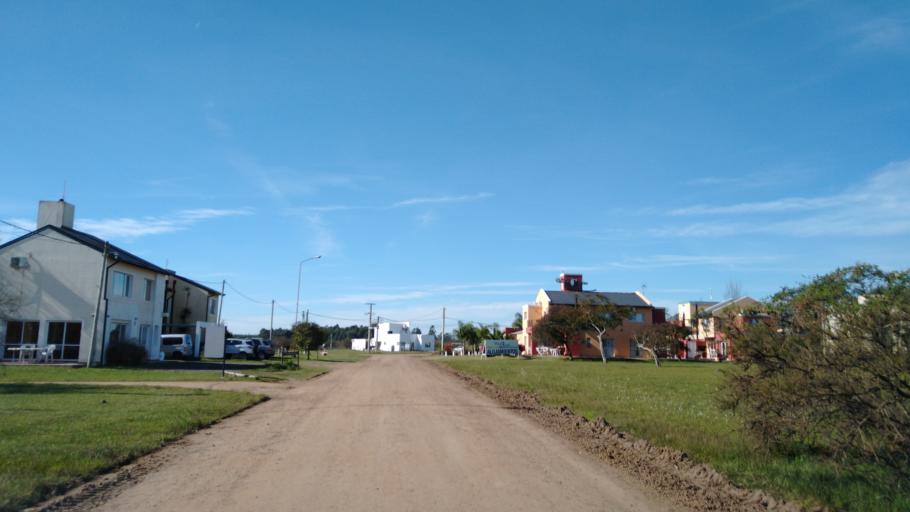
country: AR
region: Entre Rios
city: Chajari
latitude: -30.7424
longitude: -58.0114
